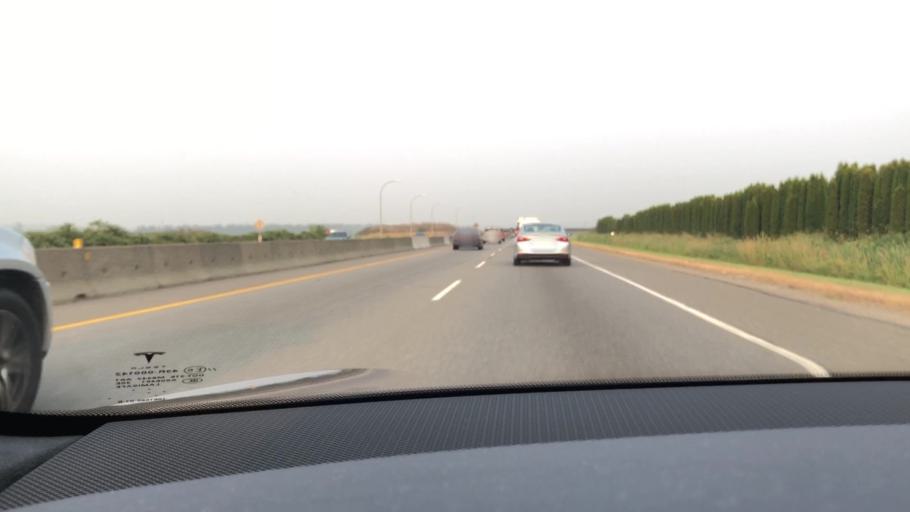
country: CA
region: British Columbia
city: Ladner
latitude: 49.1767
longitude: -123.0226
